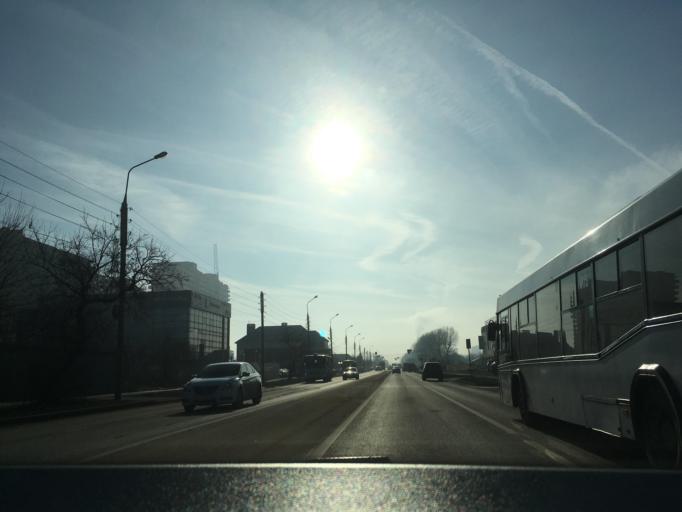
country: RU
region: Krasnodarskiy
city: Krasnodar
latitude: 45.1086
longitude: 39.0124
